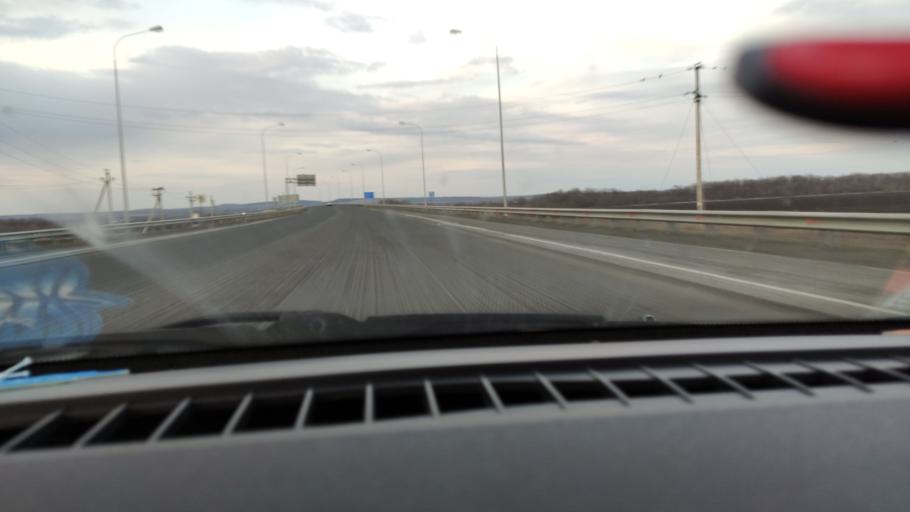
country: RU
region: Saratov
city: Yelshanka
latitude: 51.8012
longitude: 46.1885
